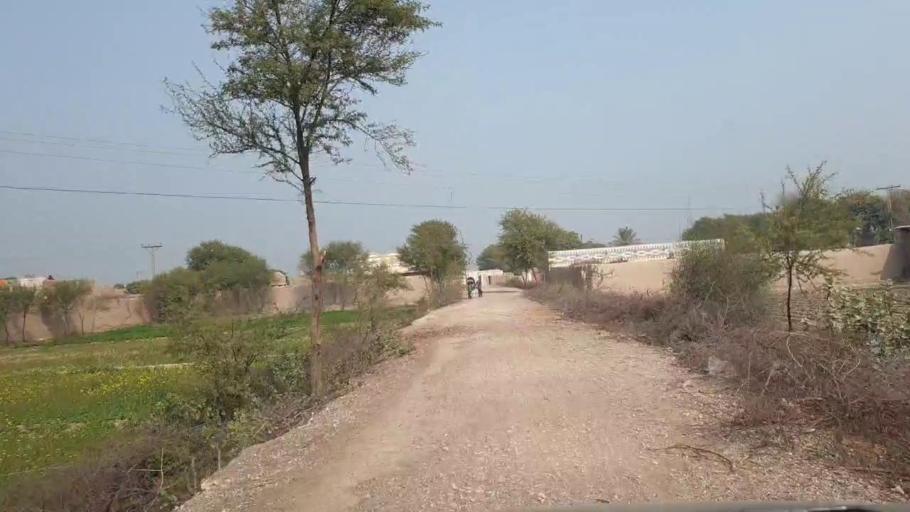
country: PK
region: Sindh
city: Bhit Shah
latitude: 25.8462
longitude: 68.4764
